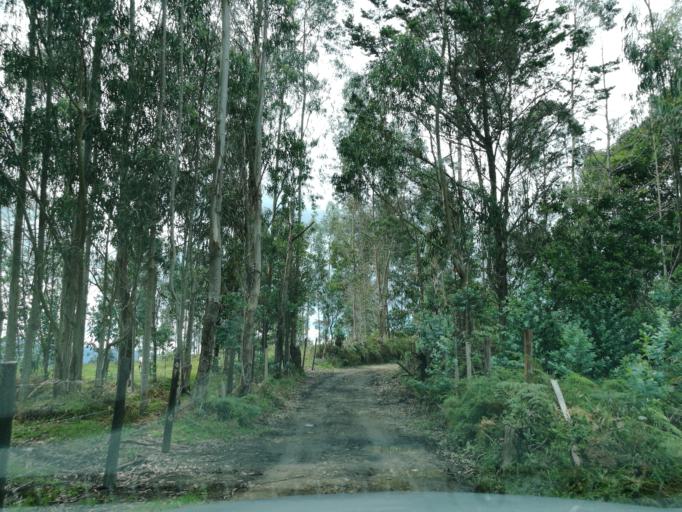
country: CO
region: Boyaca
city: Arcabuco
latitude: 5.7496
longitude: -73.4653
